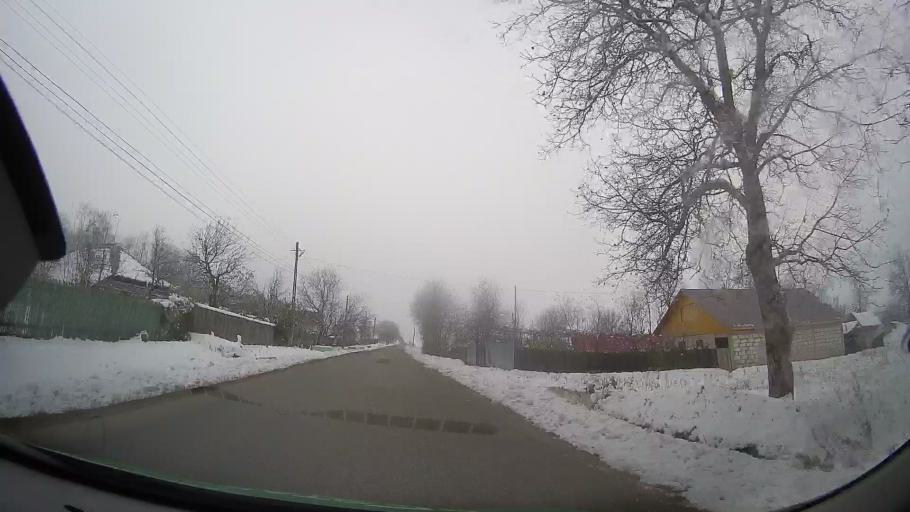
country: RO
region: Bacau
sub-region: Comuna Stanisesti
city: Stanisesti
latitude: 46.4165
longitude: 27.2685
